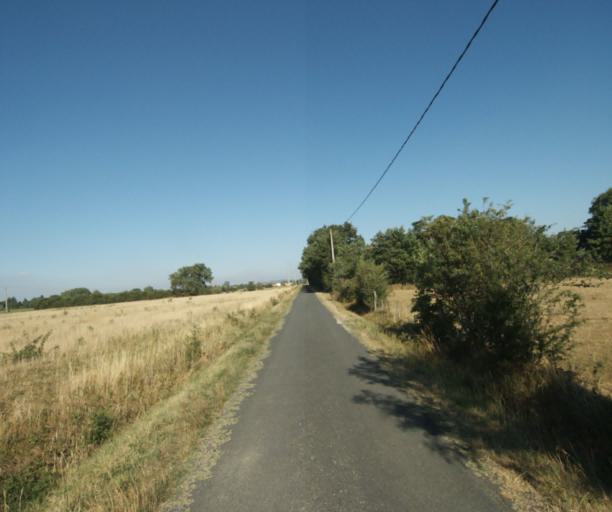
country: FR
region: Midi-Pyrenees
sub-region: Departement de la Haute-Garonne
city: Revel
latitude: 43.4613
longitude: 2.0268
